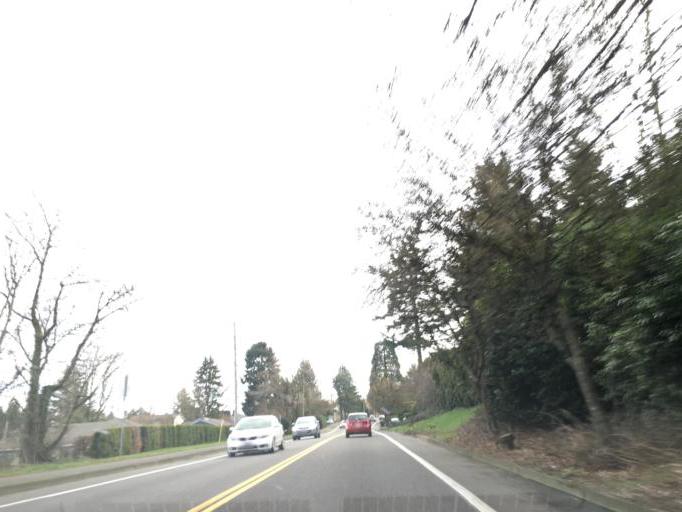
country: US
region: Oregon
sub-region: Clackamas County
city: Lake Oswego
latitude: 45.4663
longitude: -122.6835
